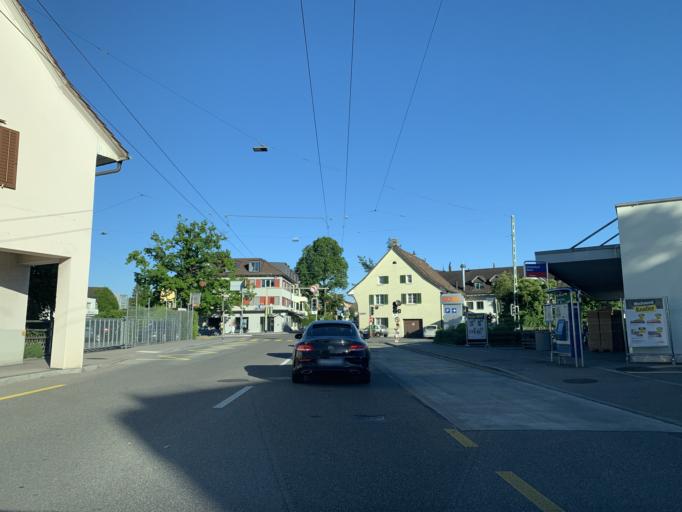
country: CH
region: Zurich
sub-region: Bezirk Winterthur
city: Seen (Kreis 3) / Waldegg
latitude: 47.4849
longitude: 8.7589
